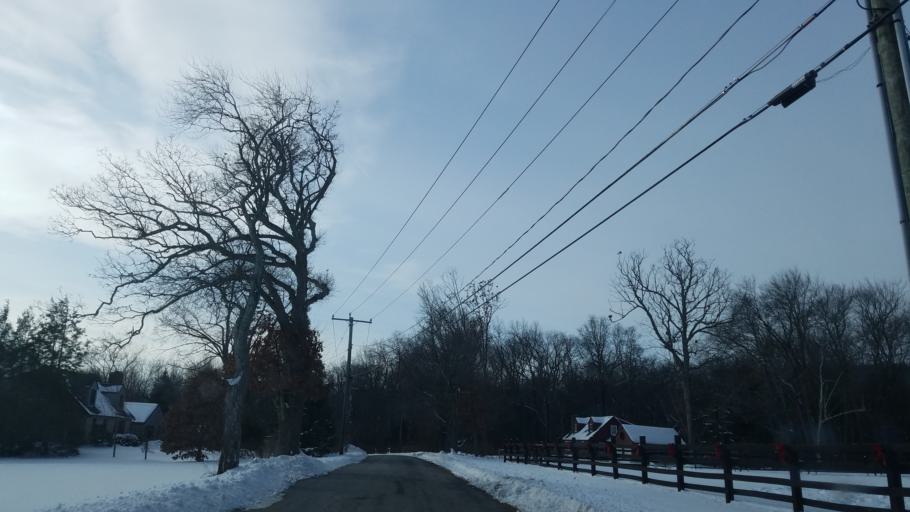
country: US
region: Connecticut
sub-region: Hartford County
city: Canton Valley
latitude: 41.8464
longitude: -72.9062
